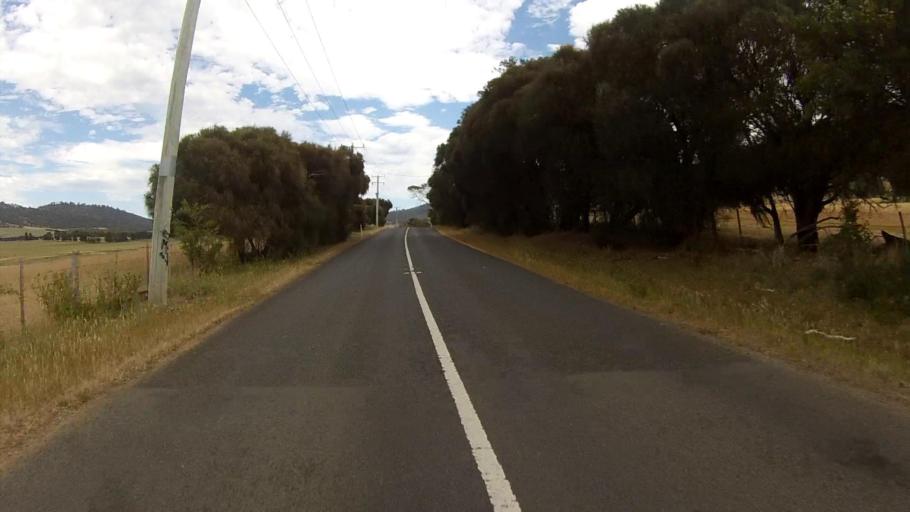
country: AU
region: Tasmania
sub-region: Clarence
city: Cambridge
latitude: -42.7295
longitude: 147.4008
